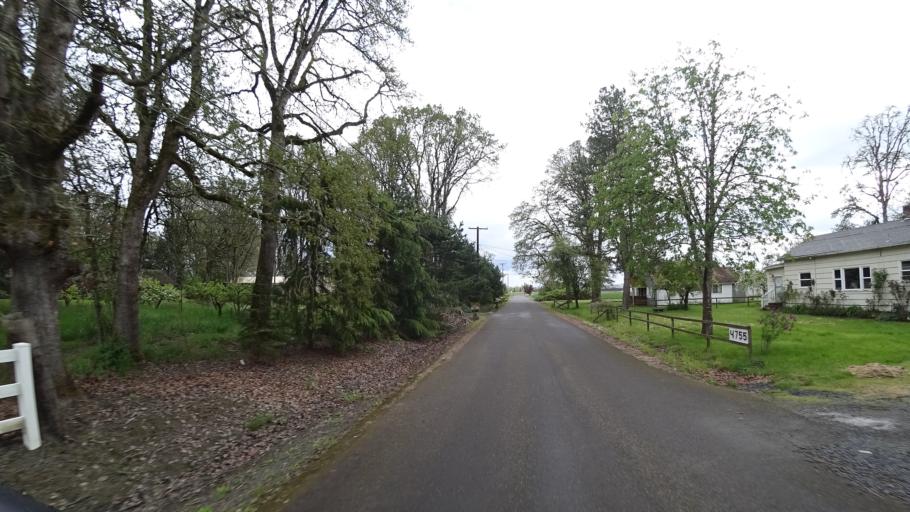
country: US
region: Oregon
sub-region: Washington County
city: Hillsboro
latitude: 45.5545
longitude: -122.9584
